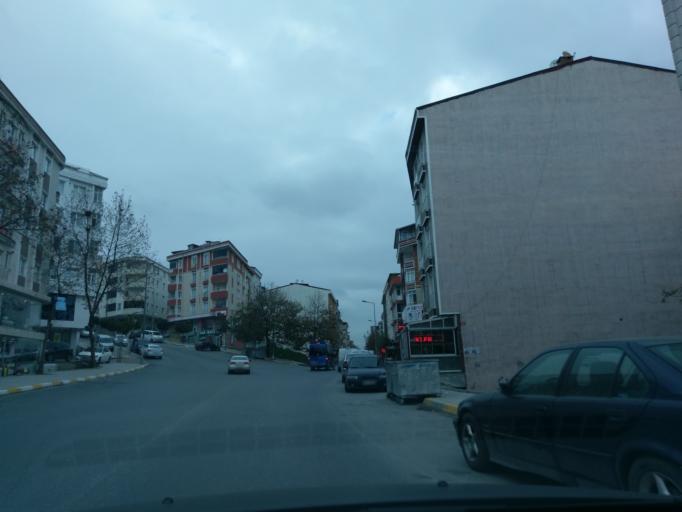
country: TR
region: Istanbul
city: Esenyurt
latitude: 41.0133
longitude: 28.6669
